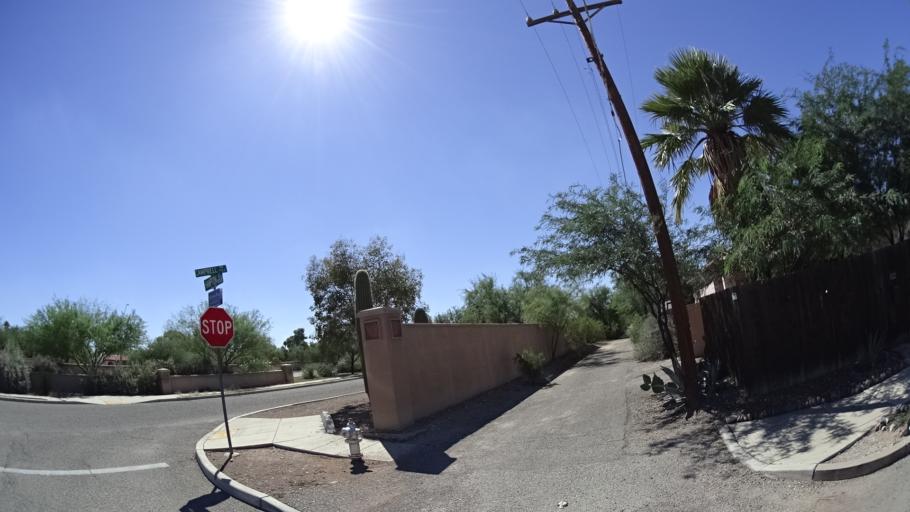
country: US
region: Arizona
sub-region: Pima County
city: Tucson
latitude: 32.2478
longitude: -110.9446
